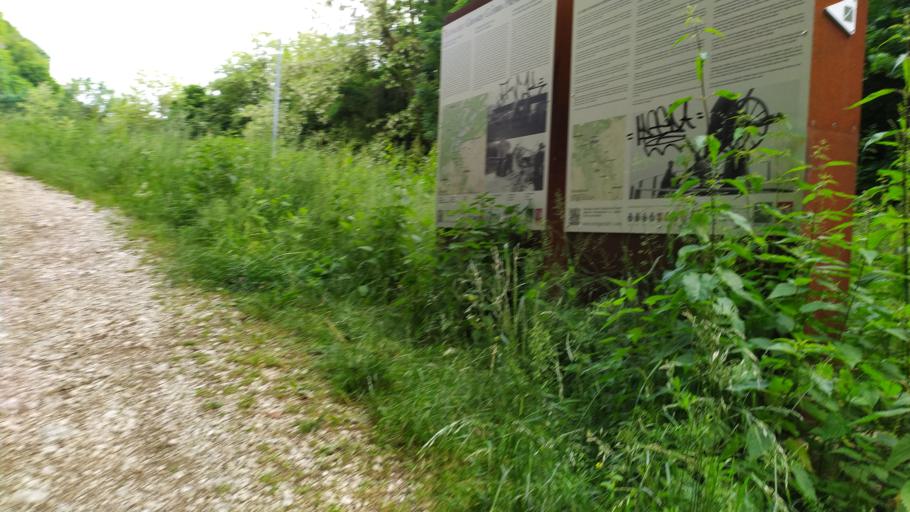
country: IT
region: Veneto
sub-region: Provincia di Vicenza
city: Torrebelvicino
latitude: 45.6835
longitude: 11.3099
